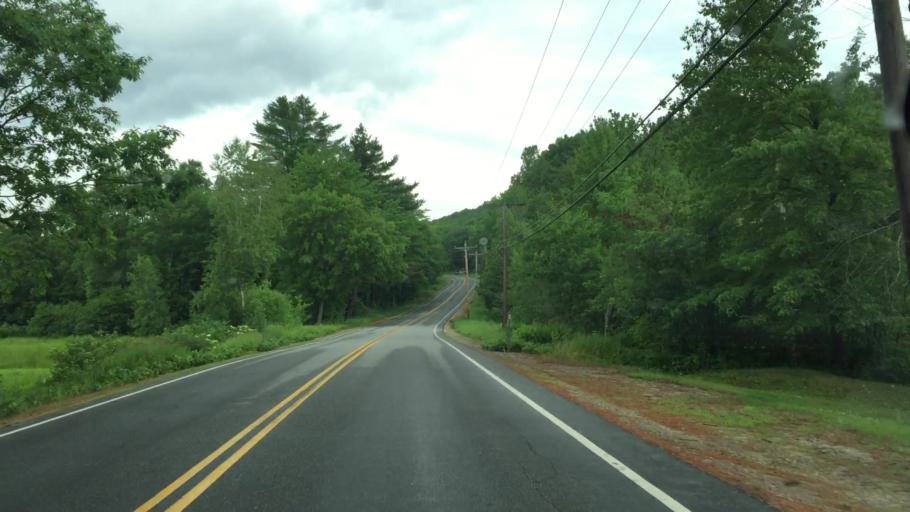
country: US
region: New Hampshire
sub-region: Carroll County
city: Center Harbor
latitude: 43.7434
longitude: -71.4781
